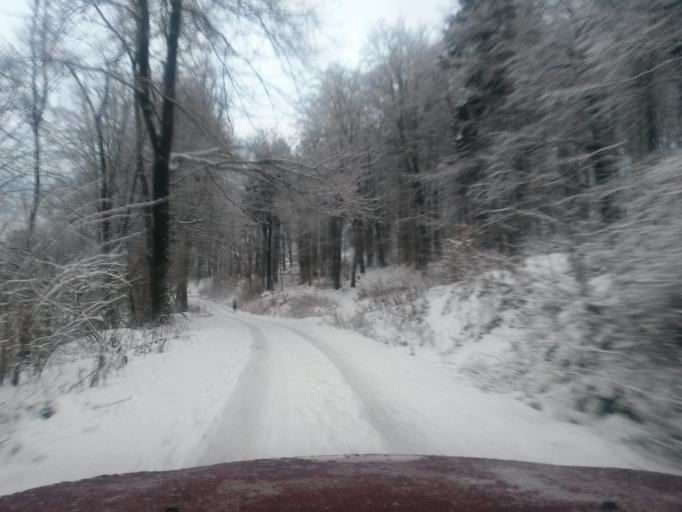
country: SK
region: Kosicky
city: Kosice
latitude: 48.7610
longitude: 21.1215
